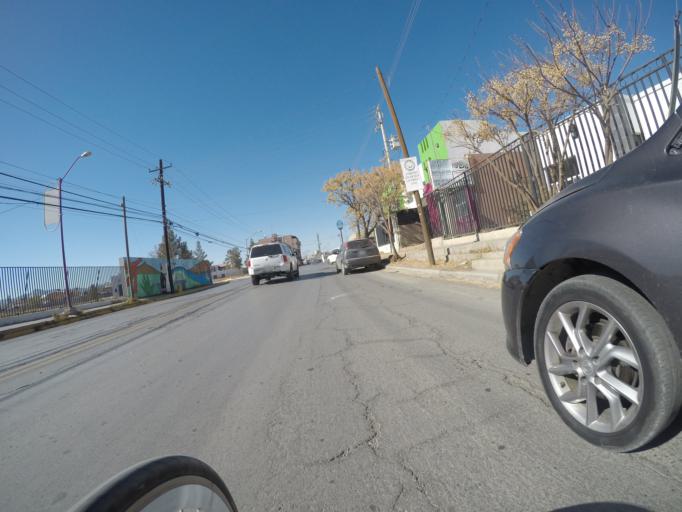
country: MX
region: Chihuahua
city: Ciudad Juarez
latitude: 31.7126
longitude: -106.4140
